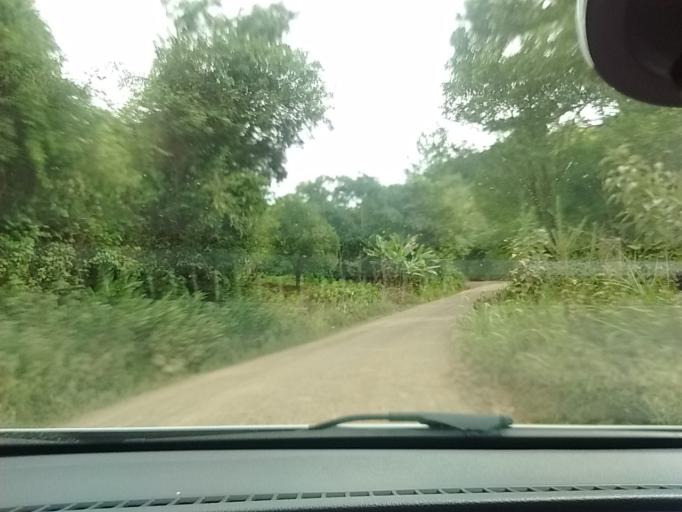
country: BR
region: Rio Grande do Sul
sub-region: Tres Coroas
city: Tres Coroas
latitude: -29.4497
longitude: -50.7597
